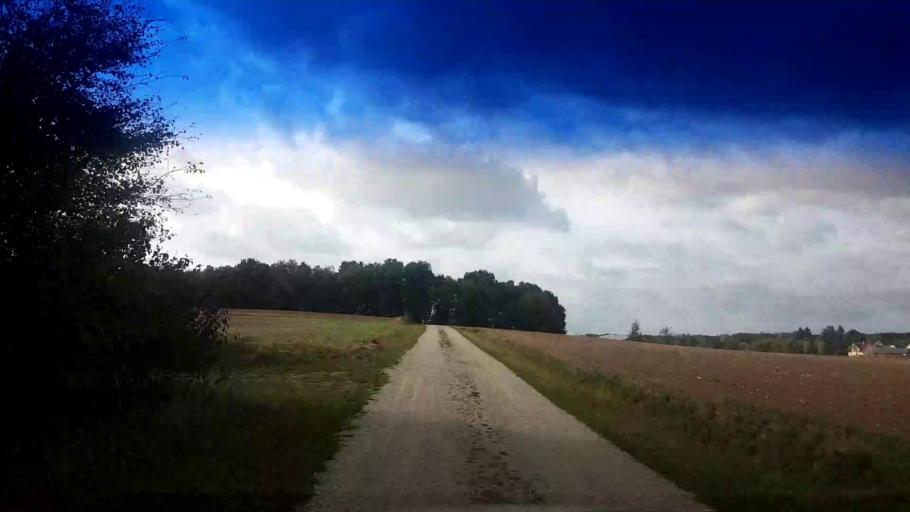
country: DE
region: Bavaria
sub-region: Upper Franconia
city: Frensdorf
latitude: 49.8283
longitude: 10.8760
